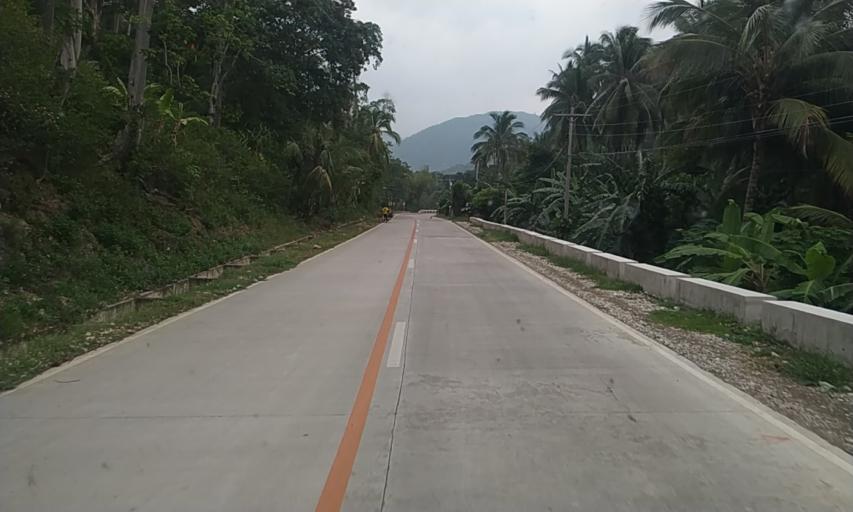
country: PH
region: Central Visayas
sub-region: Province of Negros Oriental
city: Calamba
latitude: 10.1947
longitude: 123.2953
